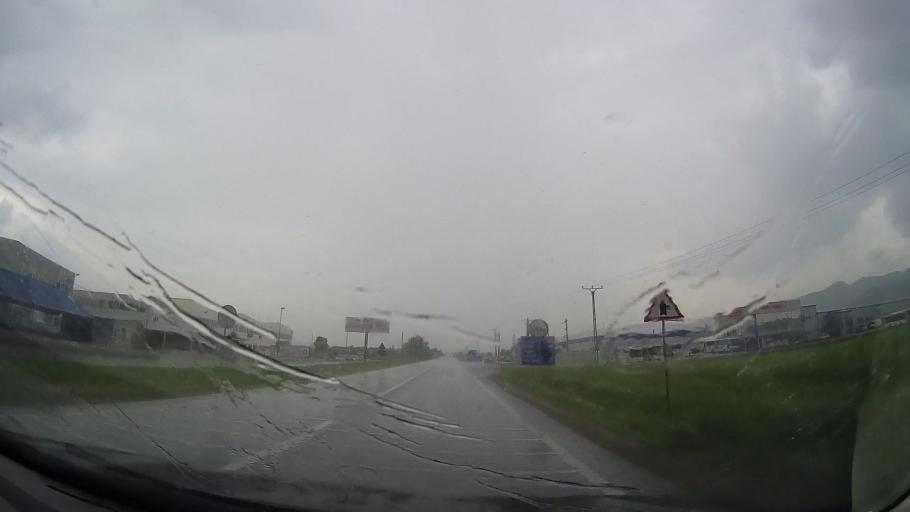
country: RO
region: Caras-Severin
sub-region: Comuna Buchin
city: Buchin
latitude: 45.3805
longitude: 22.2328
